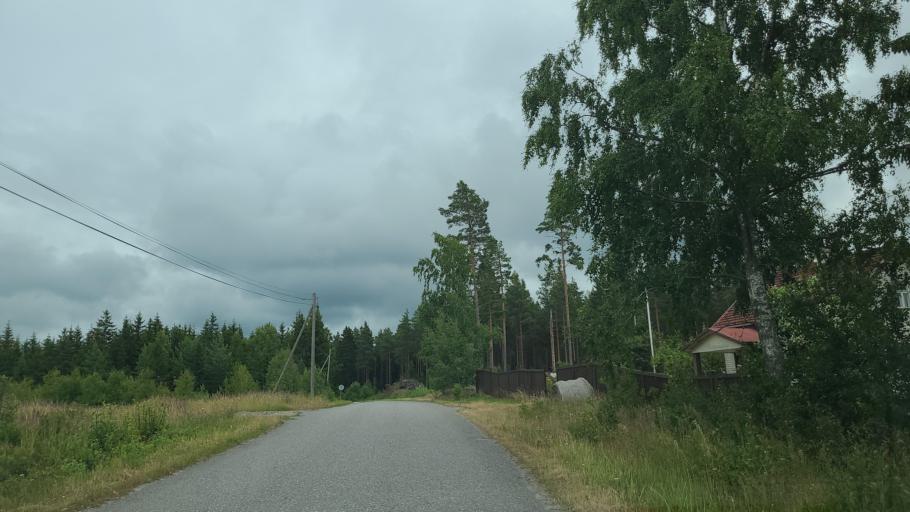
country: FI
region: Varsinais-Suomi
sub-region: Aboland-Turunmaa
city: Dragsfjaerd
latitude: 60.0808
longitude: 22.4174
